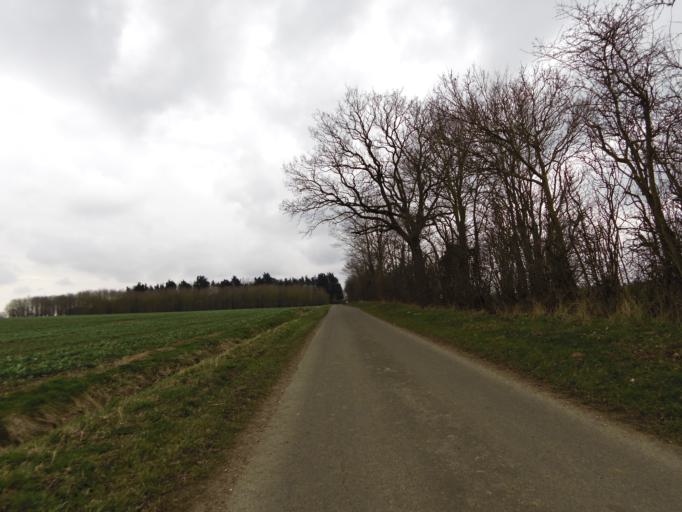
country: GB
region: England
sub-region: Suffolk
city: Halesworth
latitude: 52.3811
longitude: 1.5176
